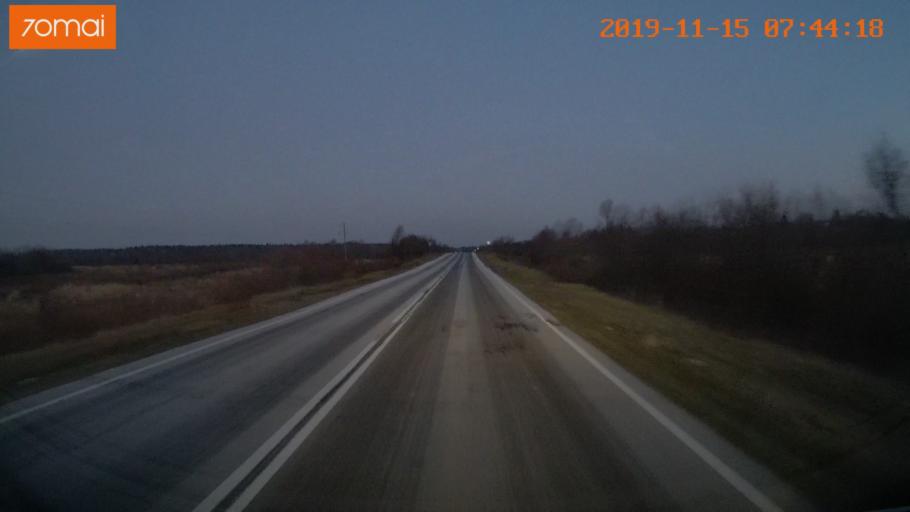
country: RU
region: Vologda
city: Sheksna
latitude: 58.8120
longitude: 38.3150
